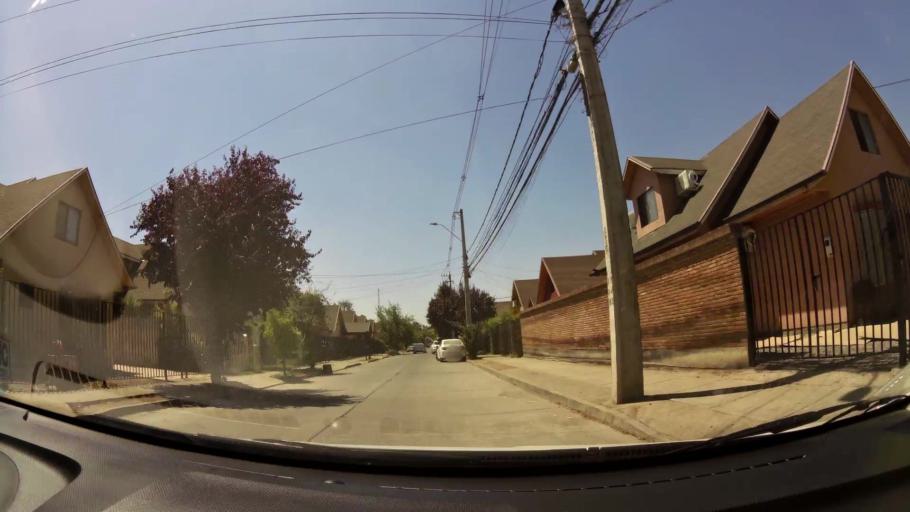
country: CL
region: Maule
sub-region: Provincia de Talca
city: Talca
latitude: -35.4268
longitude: -71.6209
